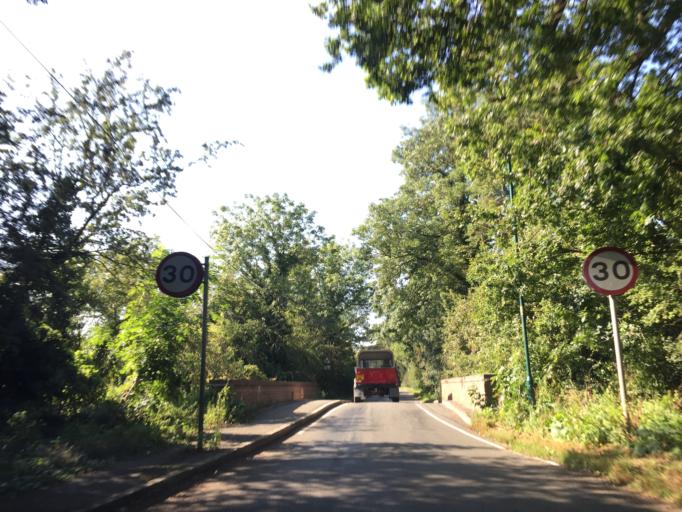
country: GB
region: England
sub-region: Leicestershire
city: Queniborough
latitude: 52.7019
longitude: -1.0351
